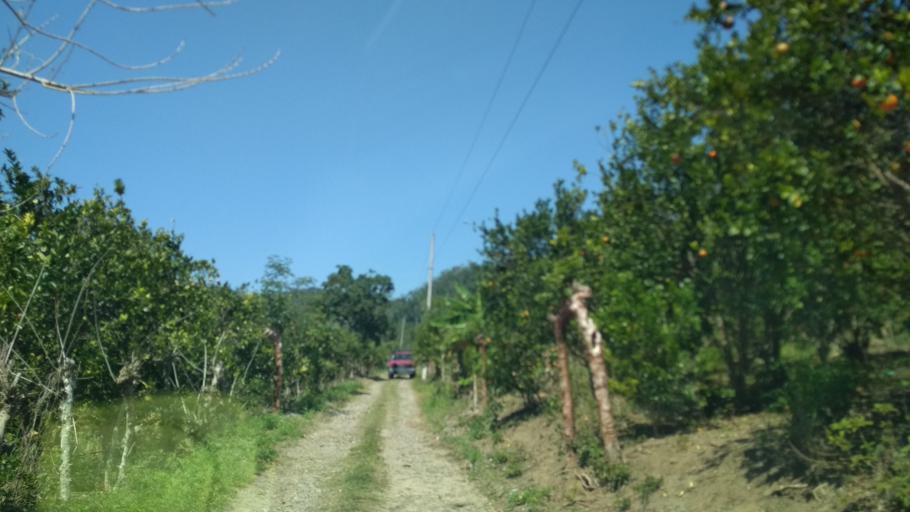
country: MX
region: Veracruz
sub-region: Papantla
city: Polutla
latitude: 20.4853
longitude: -97.2286
